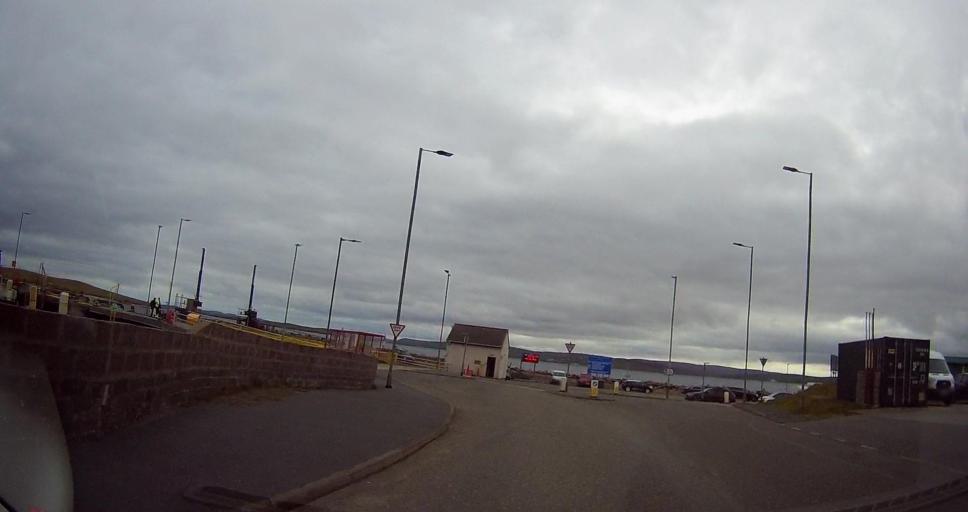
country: GB
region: Scotland
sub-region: Shetland Islands
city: Shetland
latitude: 60.4970
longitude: -1.1587
